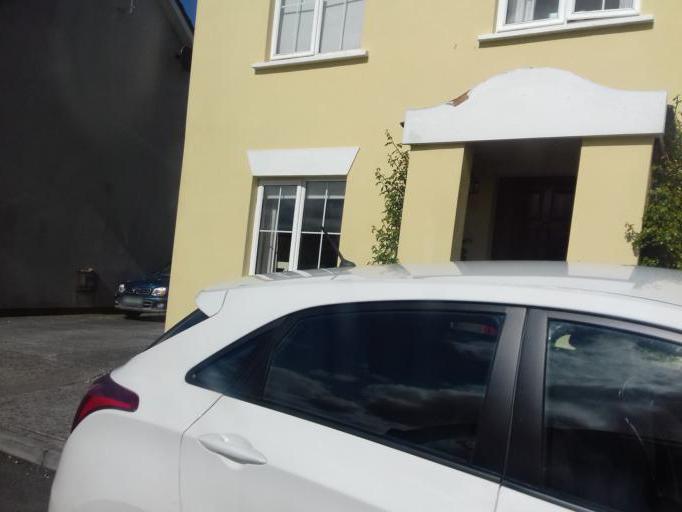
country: IE
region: Leinster
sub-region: Laois
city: Portlaoise
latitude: 53.0461
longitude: -7.2700
